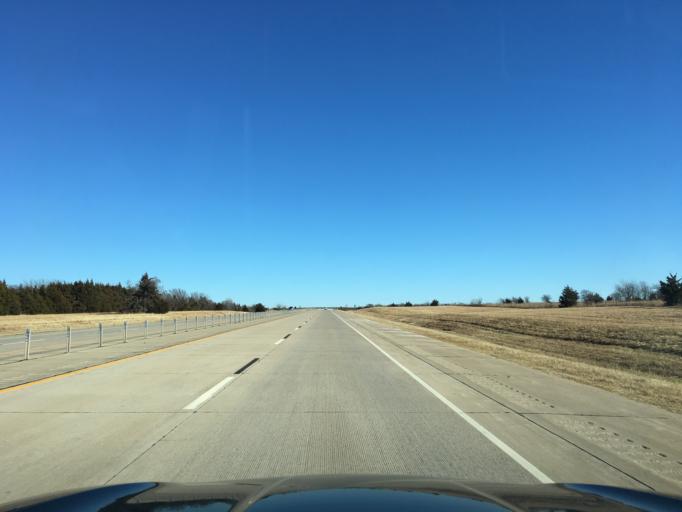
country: US
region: Oklahoma
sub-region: Payne County
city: Yale
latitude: 36.2250
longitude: -96.6719
